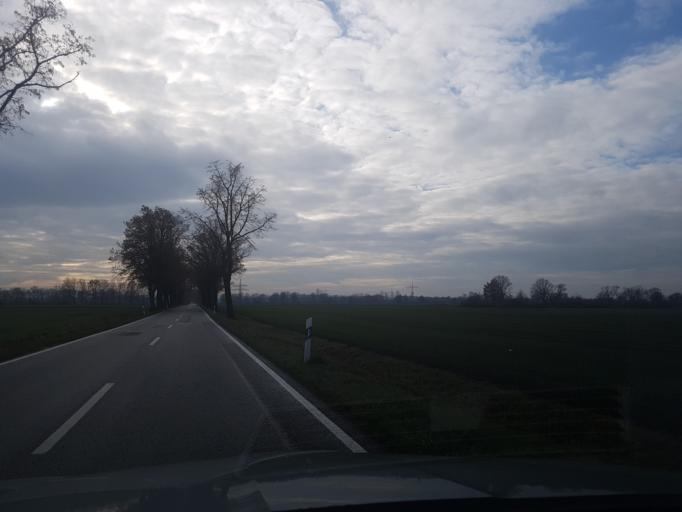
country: DE
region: Brandenburg
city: Plessa
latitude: 51.4537
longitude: 13.6228
